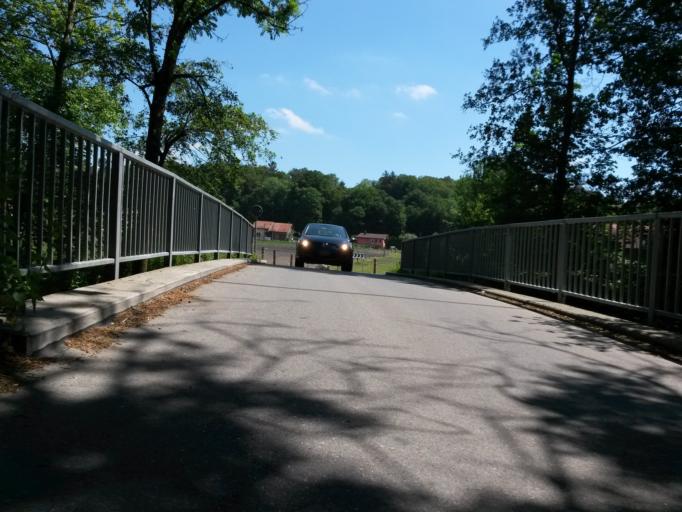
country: CH
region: Bern
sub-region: Seeland District
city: Lyss
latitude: 47.0913
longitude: 7.3112
